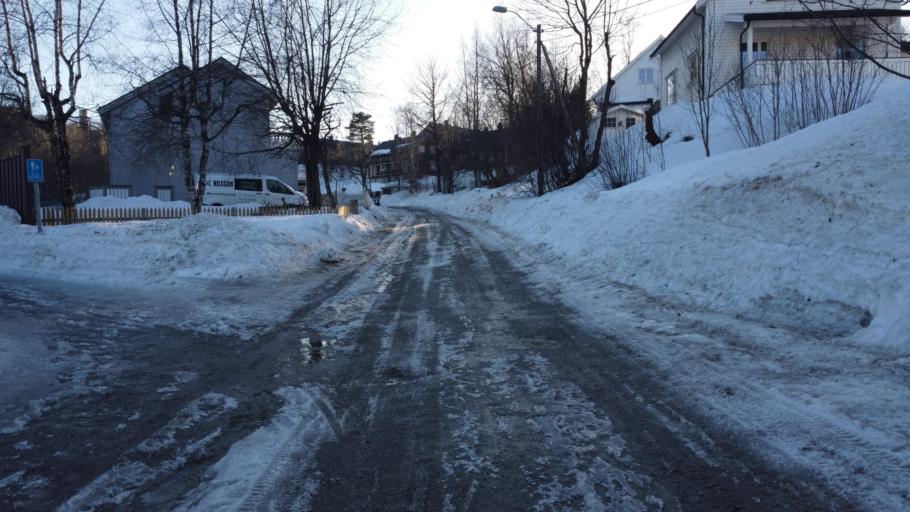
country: NO
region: Nordland
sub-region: Rana
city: Mo i Rana
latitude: 66.3164
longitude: 14.1674
